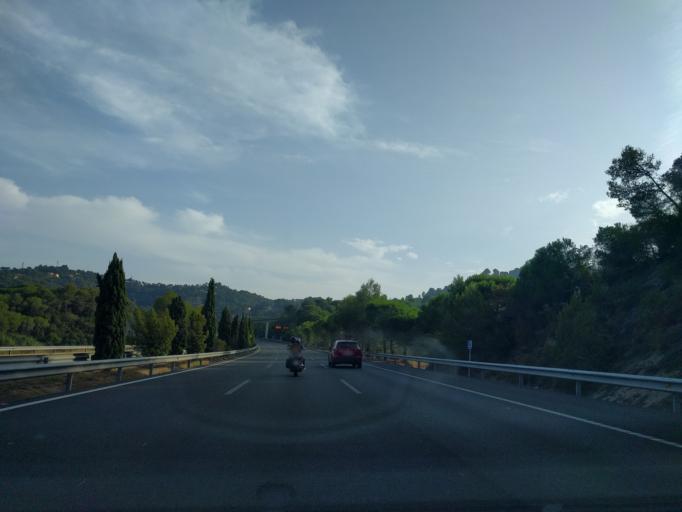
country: ES
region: Catalonia
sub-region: Provincia de Barcelona
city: Santa Susanna
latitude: 41.6646
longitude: 2.7125
